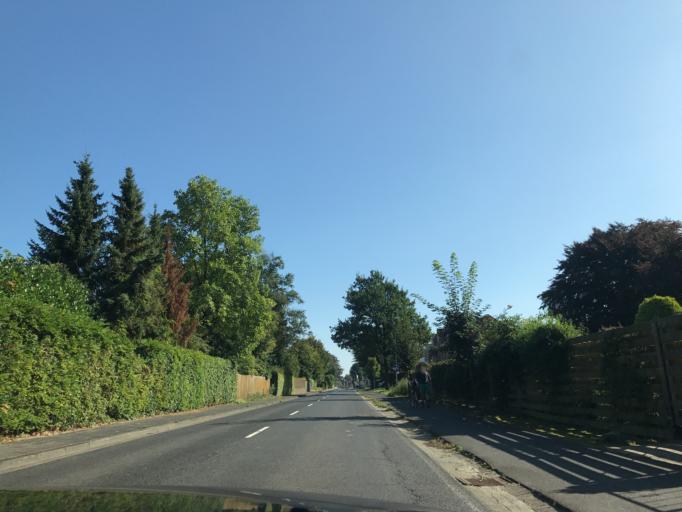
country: DE
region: Lower Saxony
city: Haselunne
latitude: 52.6693
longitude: 7.4755
